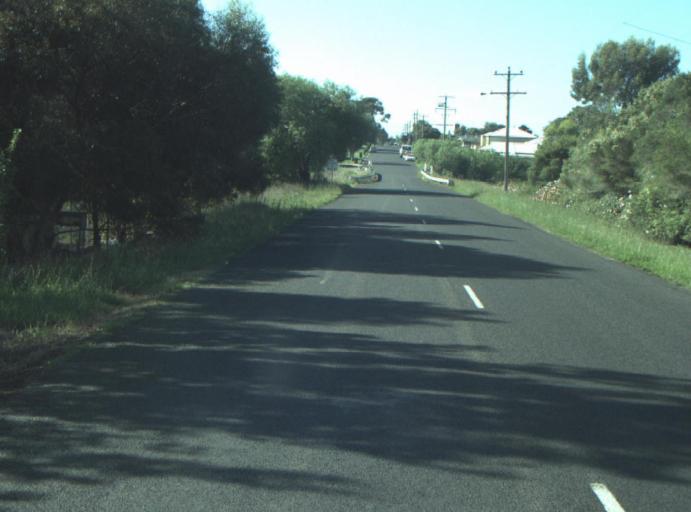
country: AU
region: Victoria
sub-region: Greater Geelong
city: Lara
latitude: -38.0136
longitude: 144.4019
